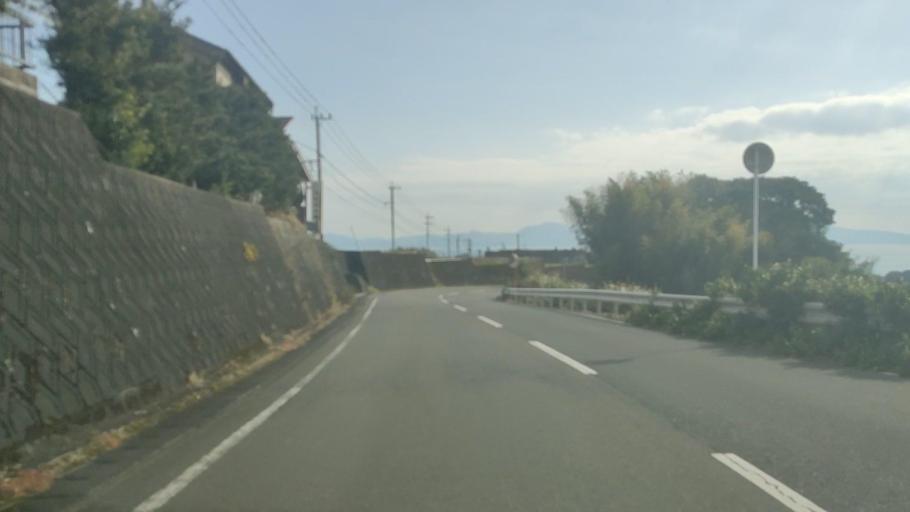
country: JP
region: Nagasaki
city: Shimabara
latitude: 32.6658
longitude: 130.2867
